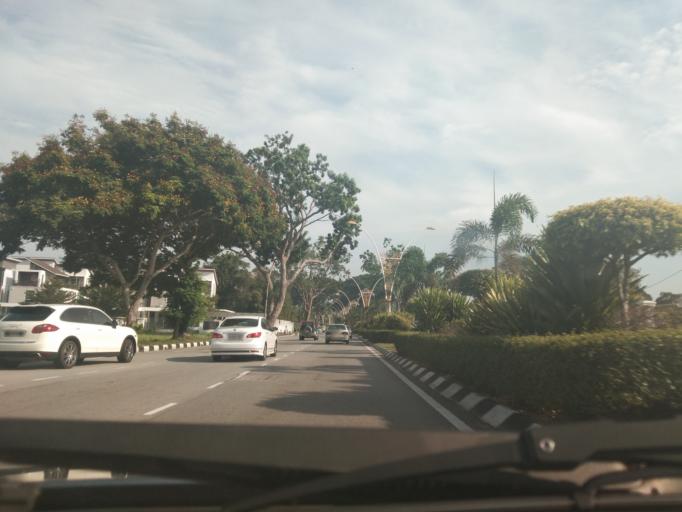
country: MY
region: Perak
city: Ipoh
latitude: 4.5847
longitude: 101.1004
